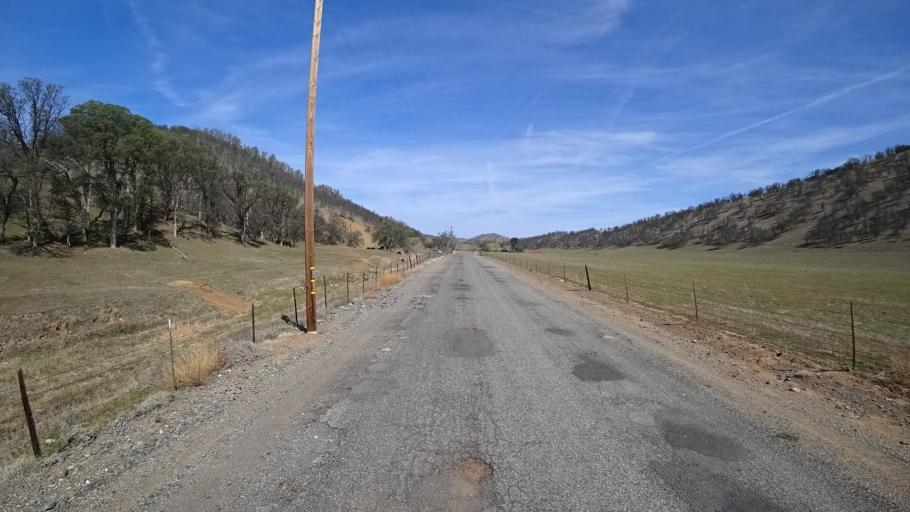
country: US
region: California
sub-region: Glenn County
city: Willows
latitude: 39.4979
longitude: -122.4543
